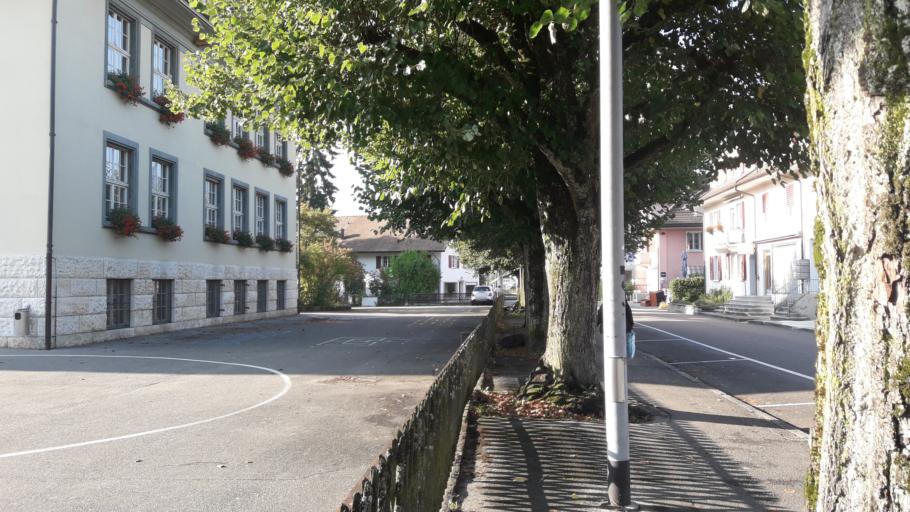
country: CH
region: Solothurn
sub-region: Bezirk Wasseramt
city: Zuchwil
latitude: 47.2045
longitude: 7.5566
